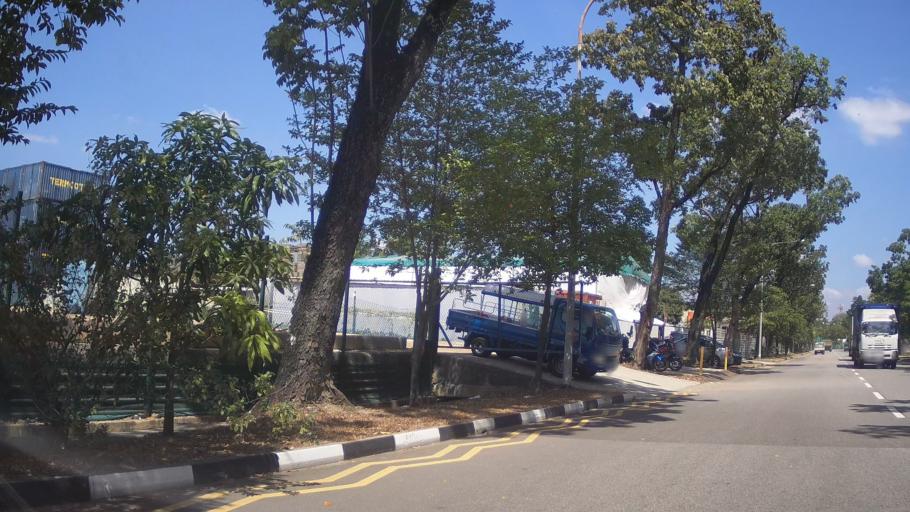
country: SG
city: Singapore
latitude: 1.3113
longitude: 103.6932
